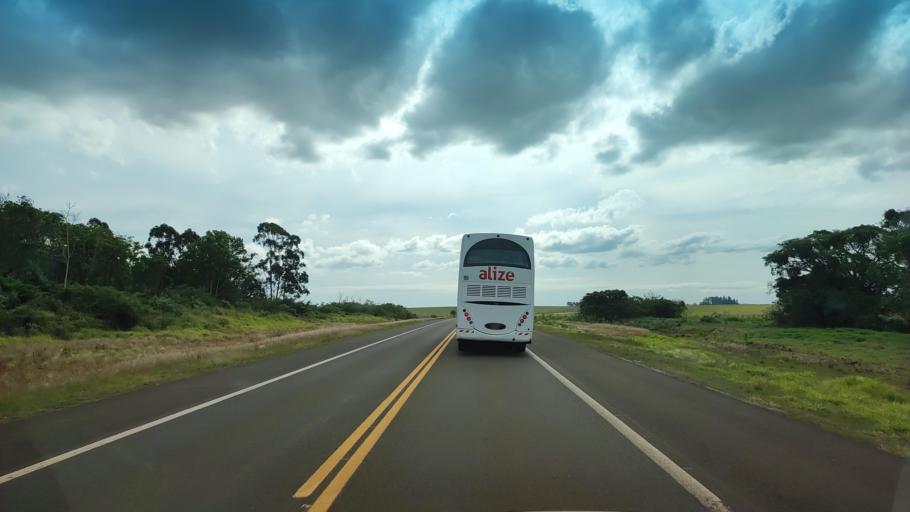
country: AR
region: Misiones
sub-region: Departamento de Capital
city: Posadas
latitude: -27.4591
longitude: -56.0049
